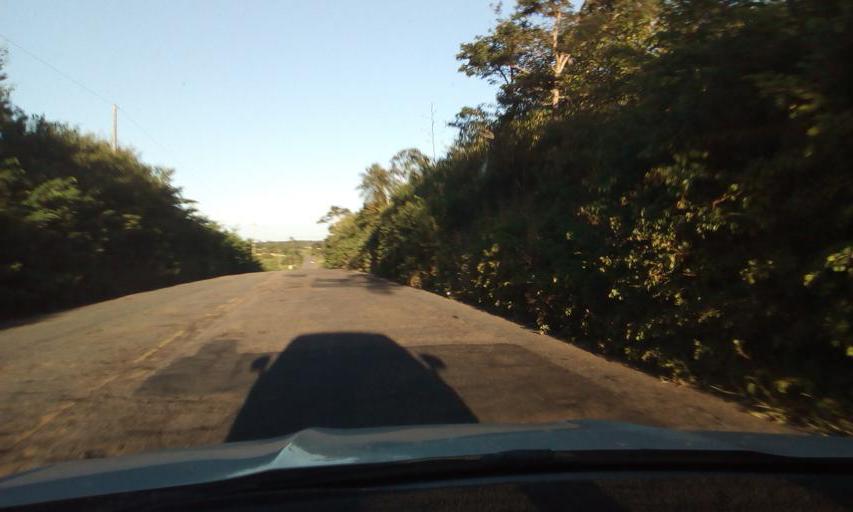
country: BR
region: Paraiba
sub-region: Areia
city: Remigio
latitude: -6.9600
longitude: -35.7785
